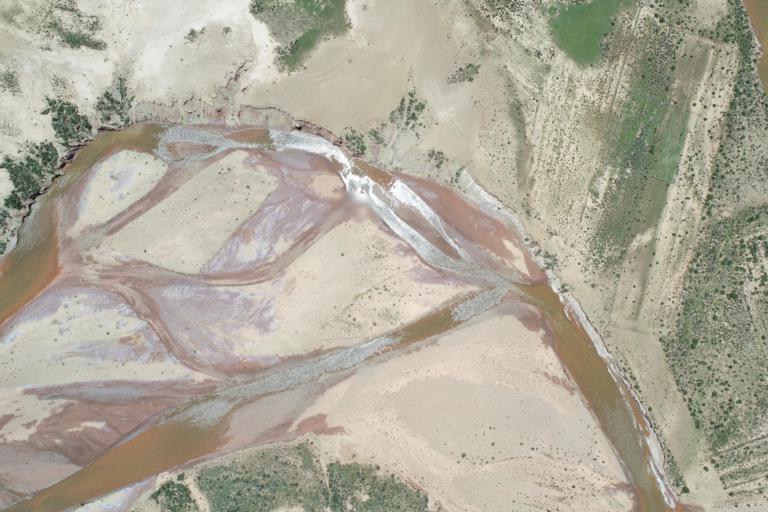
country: BO
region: La Paz
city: Curahuara de Carangas
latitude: -17.3056
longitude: -68.4949
